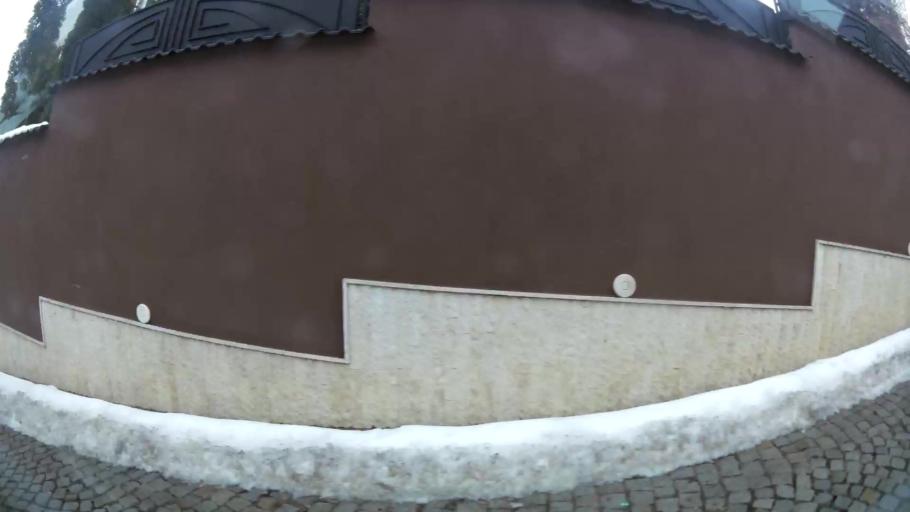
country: BG
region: Sofia-Capital
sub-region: Stolichna Obshtina
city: Sofia
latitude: 42.6437
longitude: 23.2627
